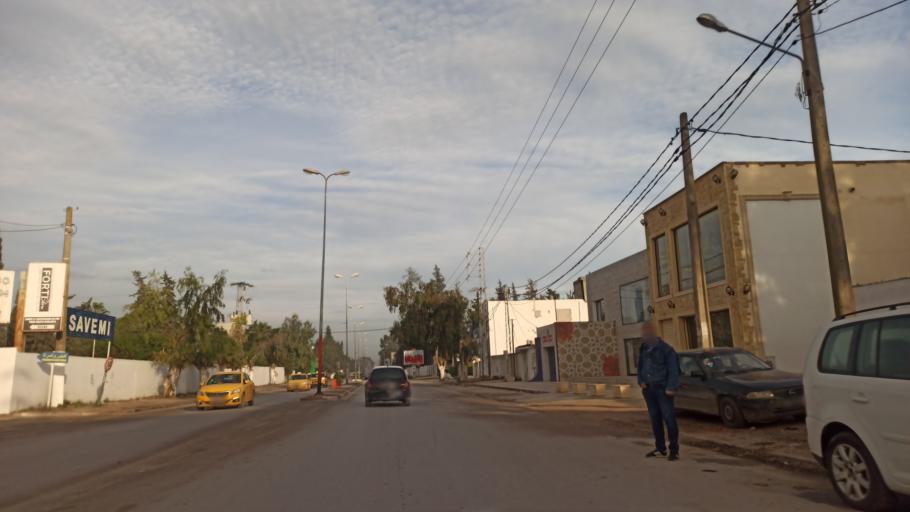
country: TN
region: Ariana
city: Ariana
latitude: 36.8675
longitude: 10.2506
